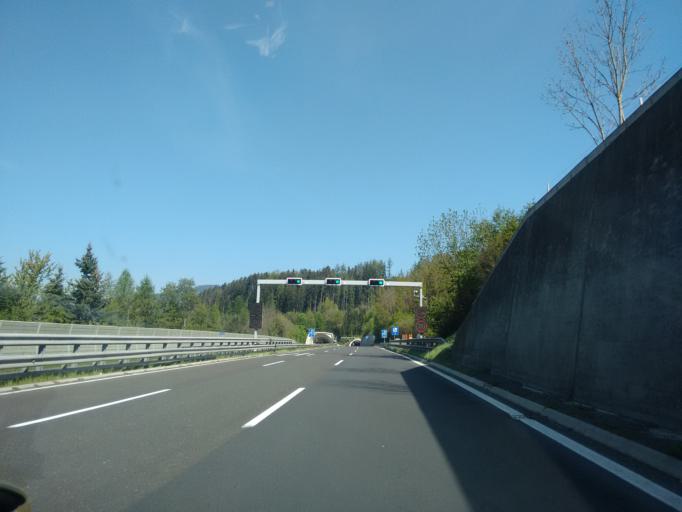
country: AT
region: Styria
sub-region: Politischer Bezirk Leoben
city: Leoben
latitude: 47.3676
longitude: 15.1066
